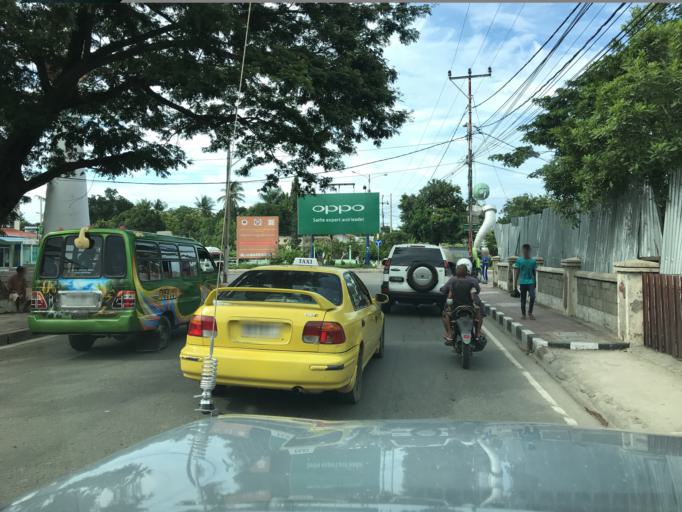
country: TL
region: Dili
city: Dili
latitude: -8.5549
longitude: 125.5690
